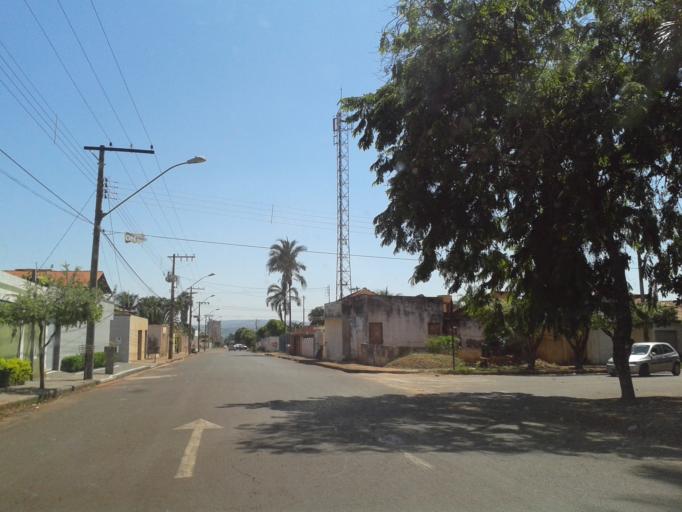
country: BR
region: Minas Gerais
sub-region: Ituiutaba
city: Ituiutaba
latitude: -18.9881
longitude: -49.4577
